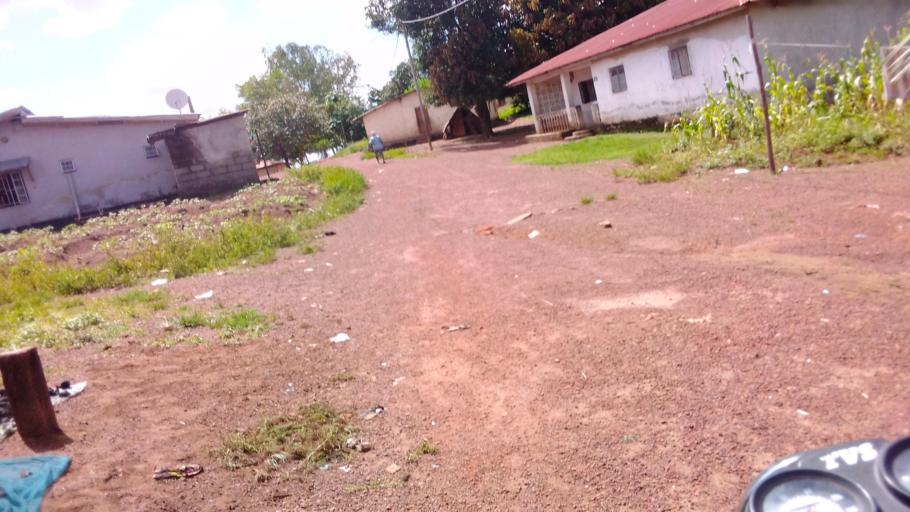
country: SL
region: Northern Province
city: Makeni
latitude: 8.8830
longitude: -12.0293
